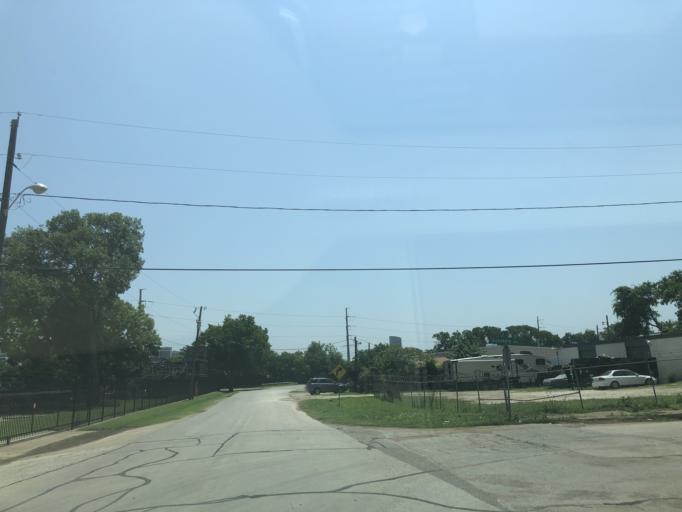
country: US
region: Texas
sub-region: Dallas County
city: Dallas
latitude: 32.8073
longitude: -96.8504
